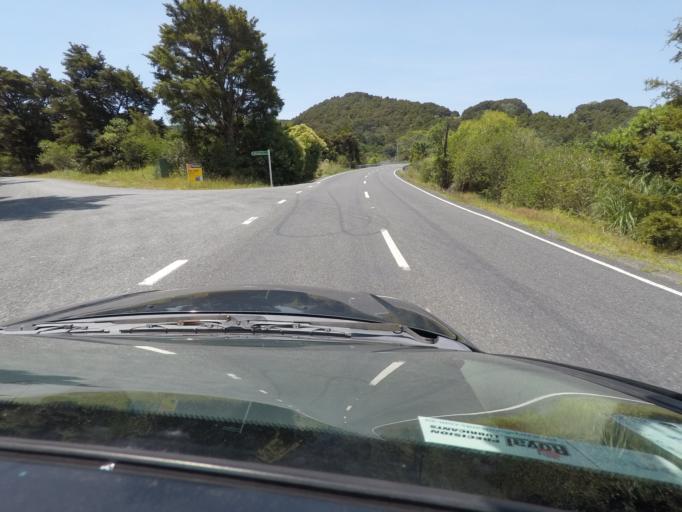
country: NZ
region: Auckland
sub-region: Auckland
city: Warkworth
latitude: -36.3136
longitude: 174.7559
